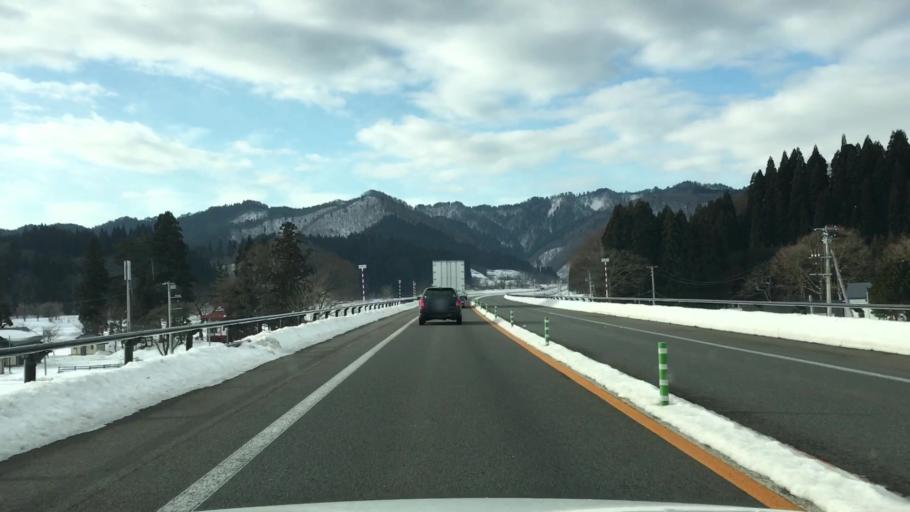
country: JP
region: Akita
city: Odate
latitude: 40.2380
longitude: 140.5029
